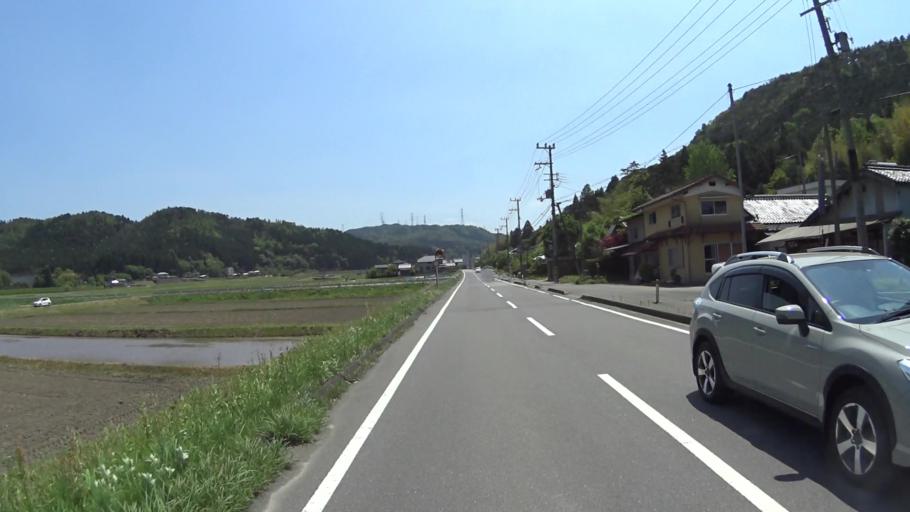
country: JP
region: Kyoto
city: Kameoka
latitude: 35.0197
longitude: 135.4875
